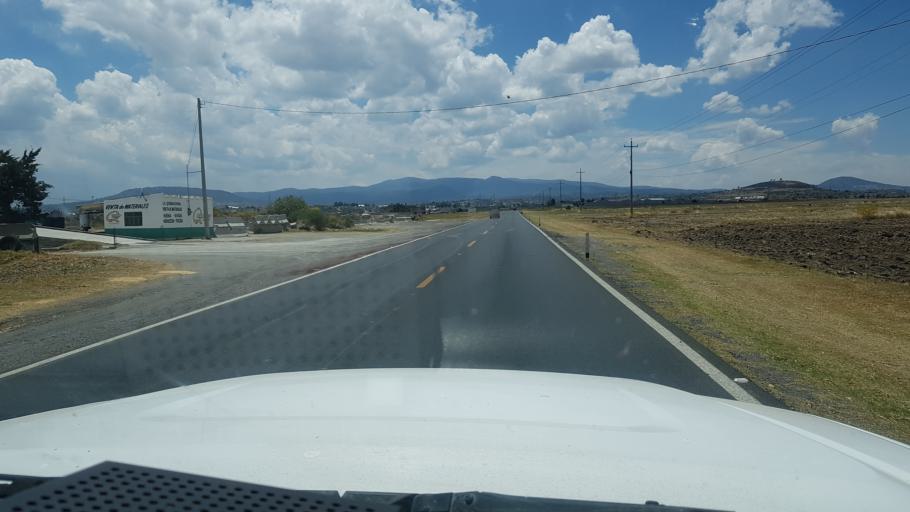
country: MX
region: Hidalgo
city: Calpulalpan
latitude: 19.6088
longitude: -98.5602
